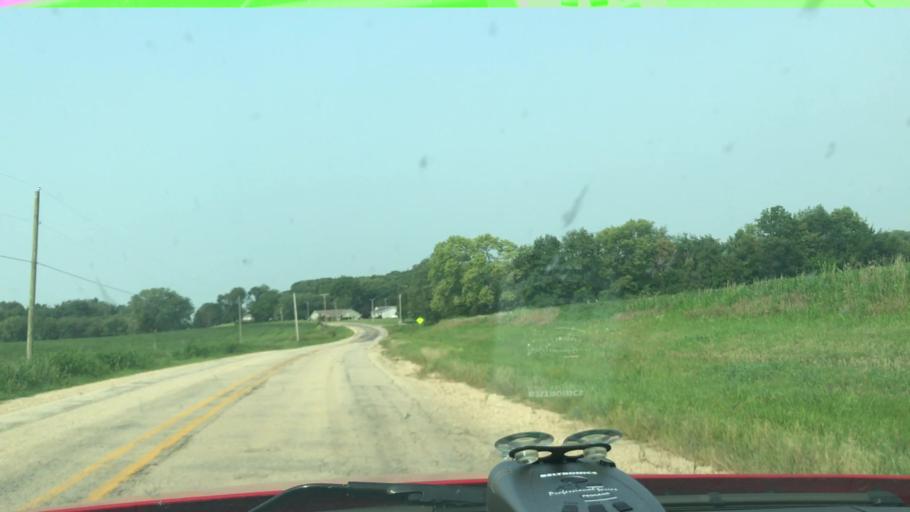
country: US
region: Illinois
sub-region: Whiteside County
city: Erie
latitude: 41.7072
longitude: -90.0842
